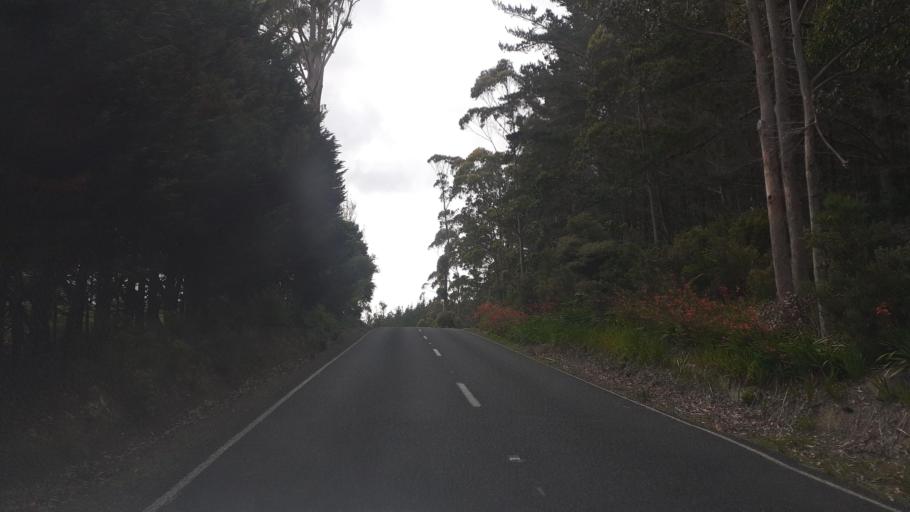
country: NZ
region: Northland
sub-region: Far North District
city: Kerikeri
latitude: -35.2169
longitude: 173.9904
